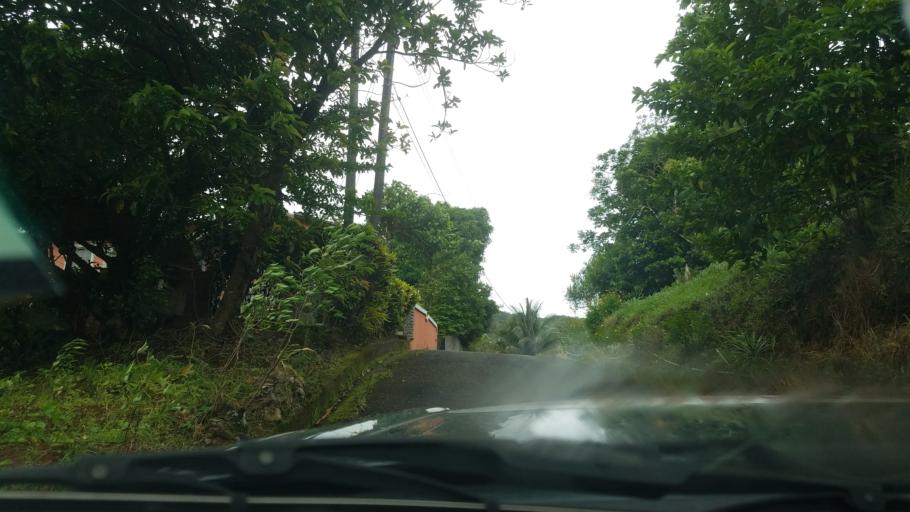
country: LC
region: Anse-la-Raye
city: Anse La Raye
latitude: 13.9242
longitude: -60.9940
